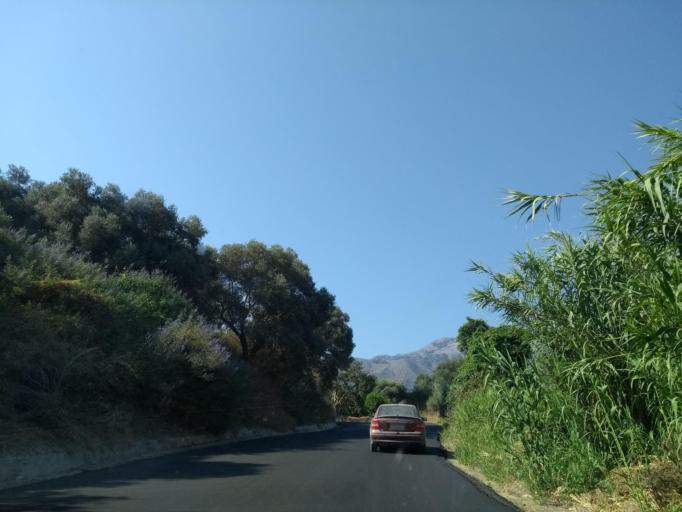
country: GR
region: Crete
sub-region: Nomos Chanias
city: Georgioupolis
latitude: 35.3267
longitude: 24.2998
